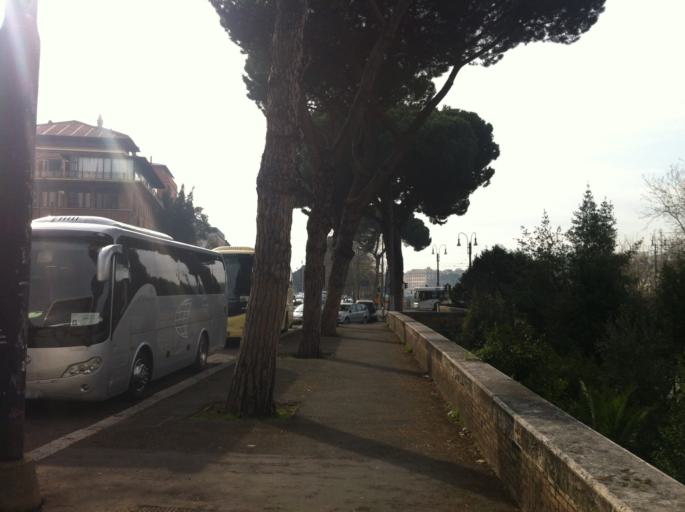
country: VA
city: Vatican City
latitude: 41.9152
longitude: 12.4714
